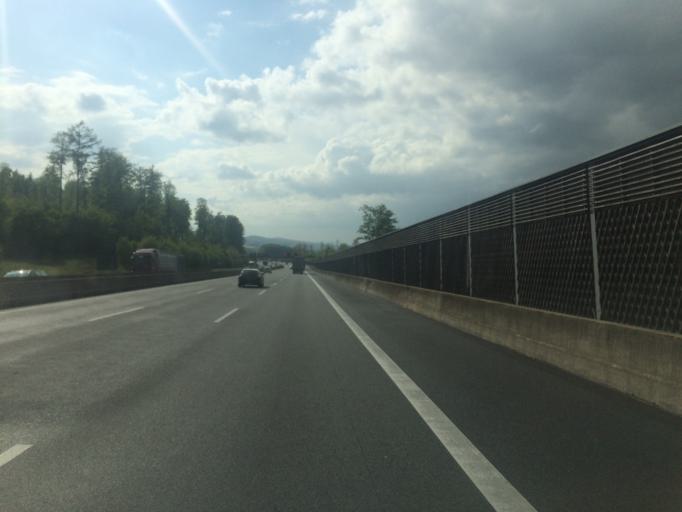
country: DE
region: Lower Saxony
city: Buchholz
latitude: 52.2187
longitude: 9.1561
